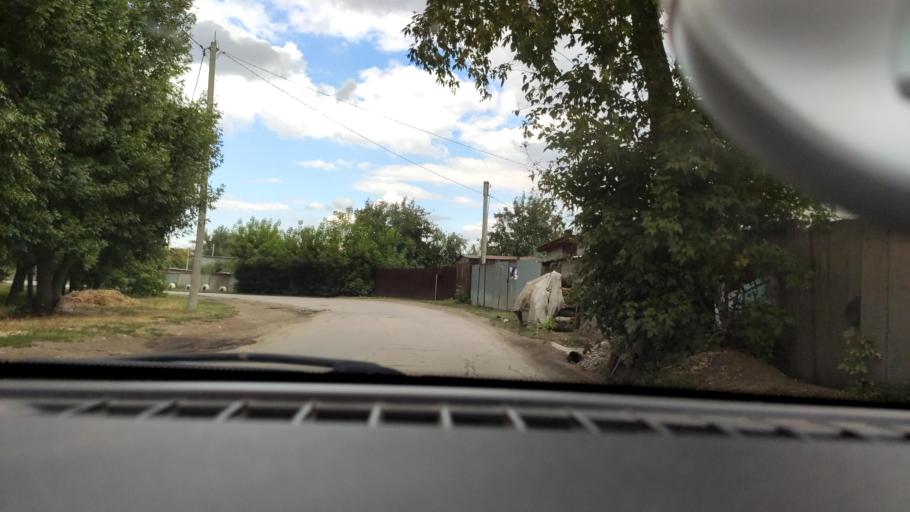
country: RU
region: Samara
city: Novokuybyshevsk
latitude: 53.1028
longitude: 50.0368
